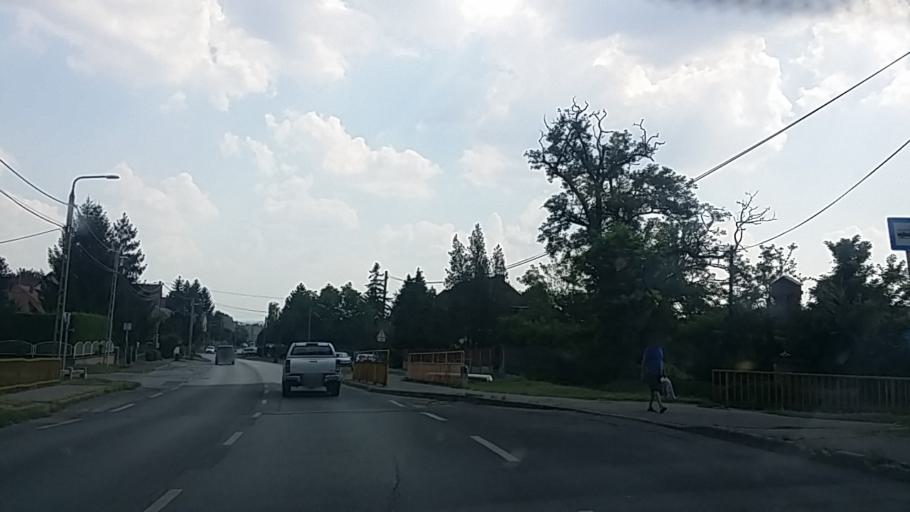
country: HU
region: Baranya
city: Pecs
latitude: 46.0728
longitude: 18.1864
